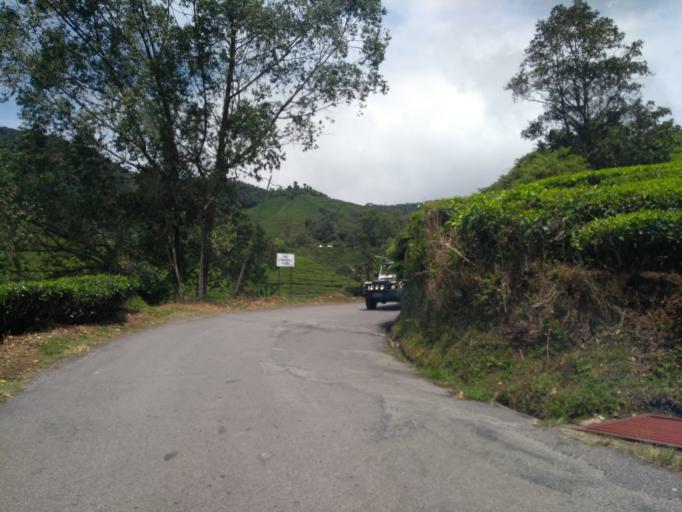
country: MY
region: Pahang
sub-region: Cameron Highlands
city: Tanah Rata
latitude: 4.5183
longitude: 101.4105
